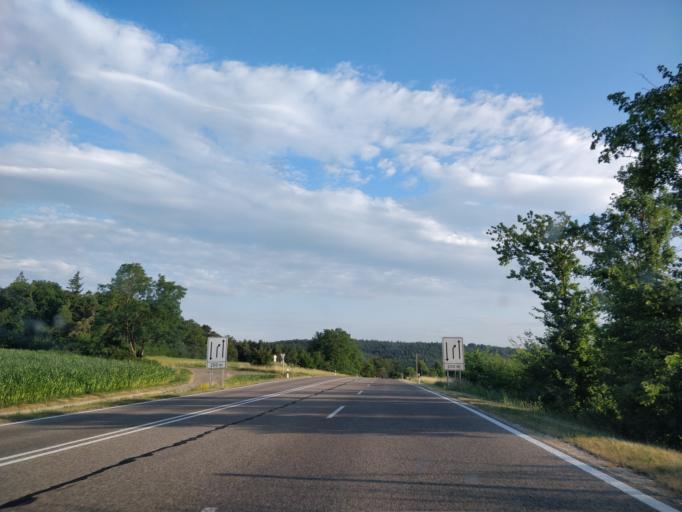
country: DE
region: Bavaria
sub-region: Swabia
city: Ederheim
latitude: 48.8167
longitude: 10.4566
